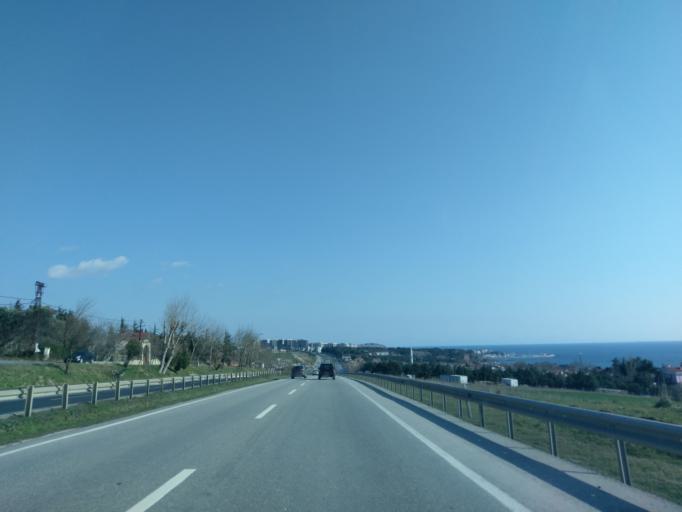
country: TR
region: Istanbul
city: Kumburgaz
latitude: 41.0133
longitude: 28.4942
